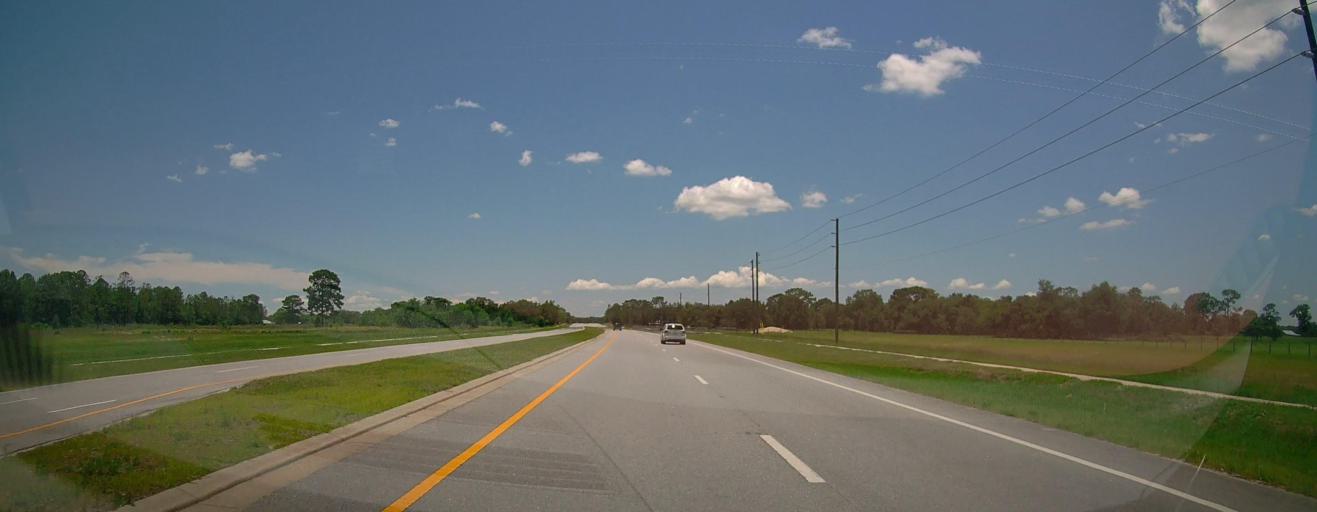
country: US
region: Florida
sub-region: Marion County
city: Belleview
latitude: 29.0516
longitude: -82.0173
